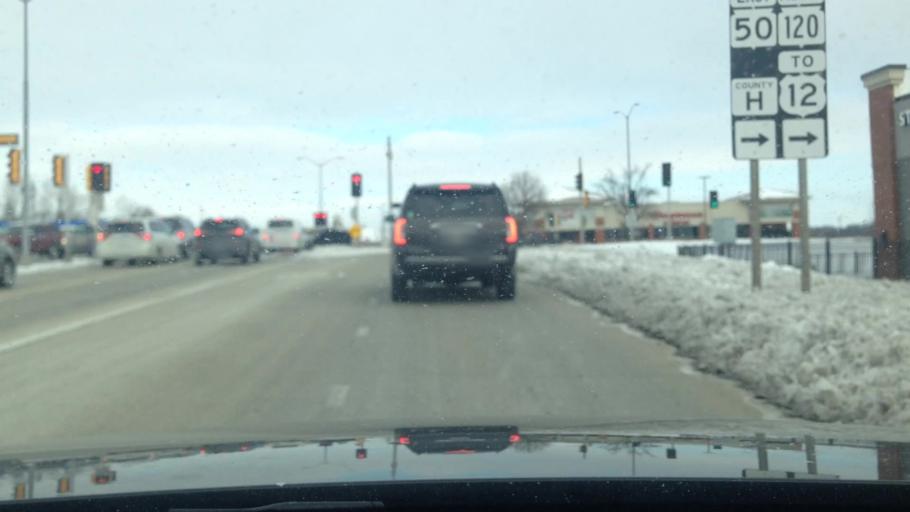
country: US
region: Wisconsin
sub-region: Walworth County
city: Lake Geneva
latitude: 42.5924
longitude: -88.4141
